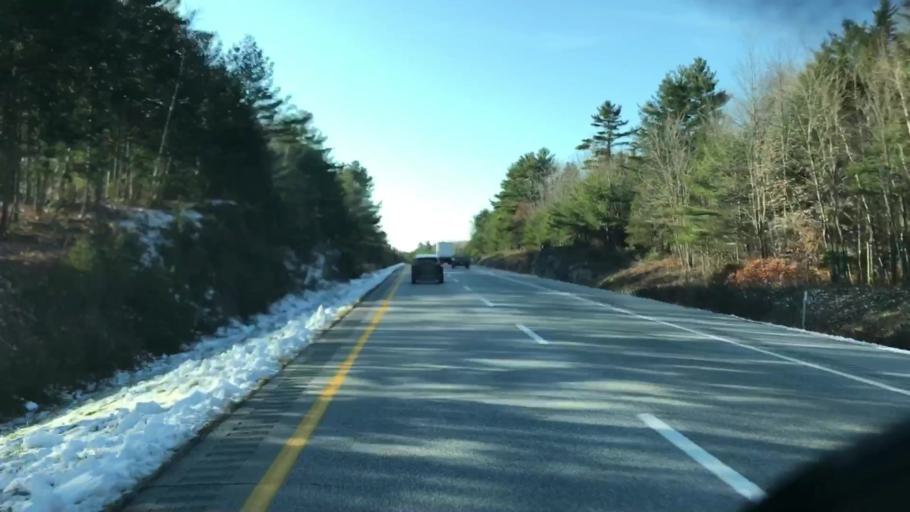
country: US
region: Maine
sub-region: Penobscot County
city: Etna
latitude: 44.7869
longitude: -69.1206
